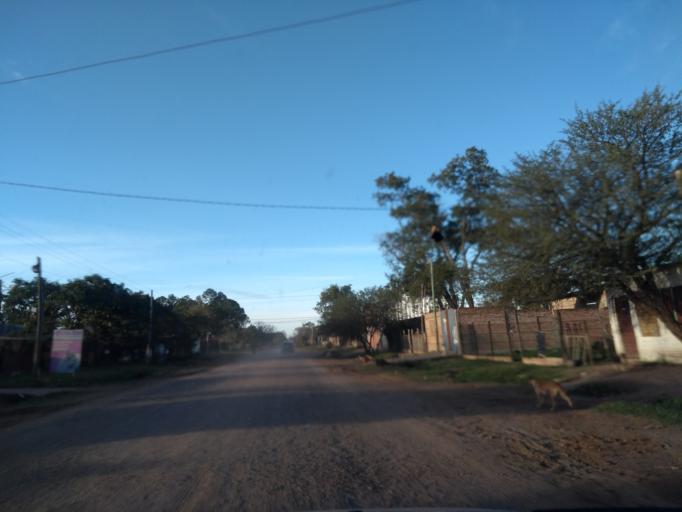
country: AR
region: Chaco
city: Resistencia
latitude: -27.4931
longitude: -58.9761
